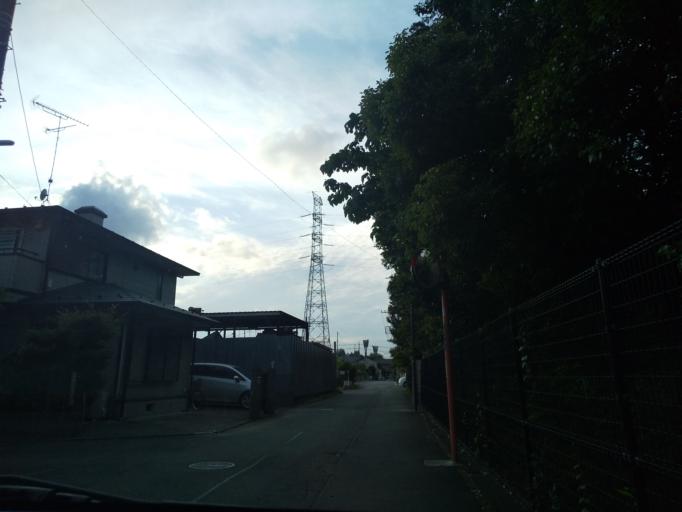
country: JP
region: Tokyo
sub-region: Machida-shi
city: Machida
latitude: 35.5498
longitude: 139.3927
